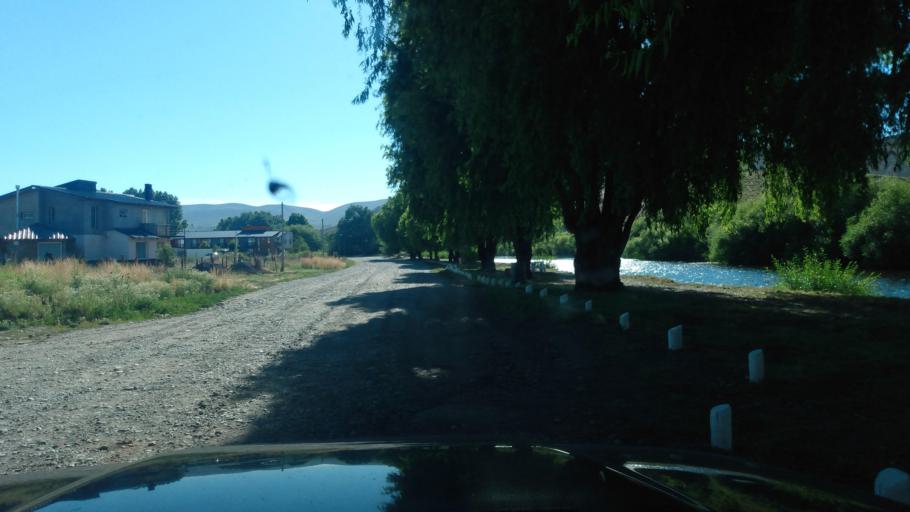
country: AR
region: Neuquen
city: Junin de los Andes
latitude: -39.9581
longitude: -71.0743
